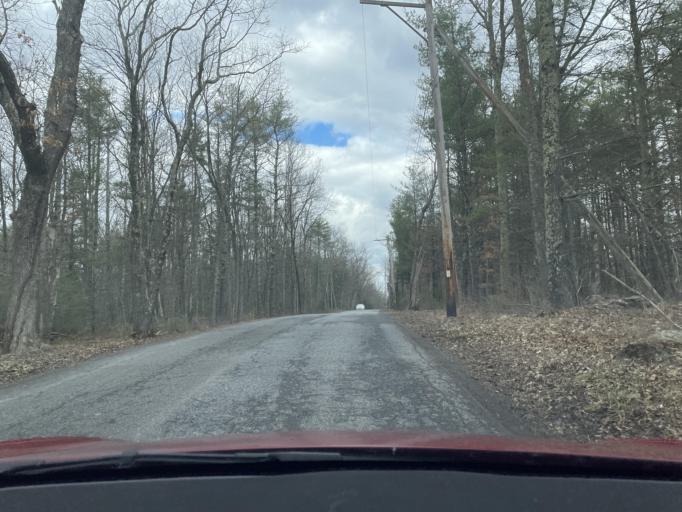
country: US
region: New York
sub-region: Ulster County
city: Zena
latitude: 42.0648
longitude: -74.0364
